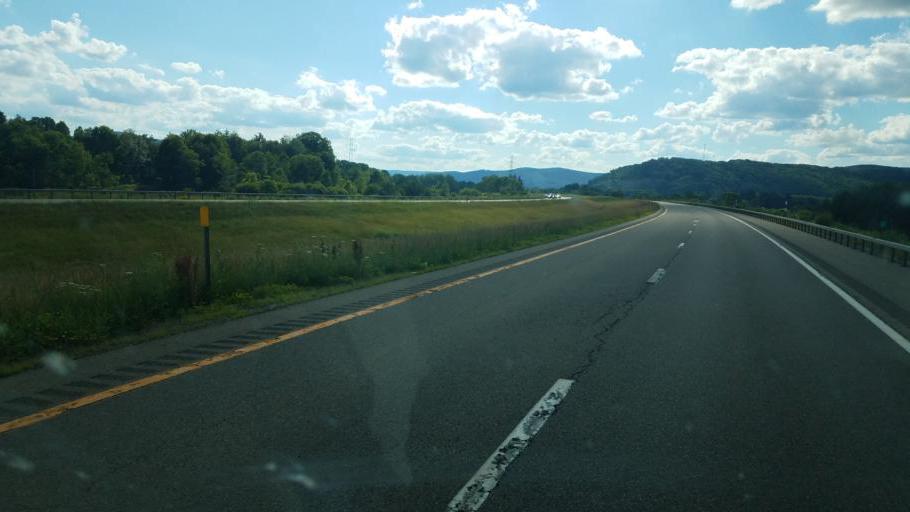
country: US
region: New York
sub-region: Cattaraugus County
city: Allegany
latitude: 42.1019
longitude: -78.4860
